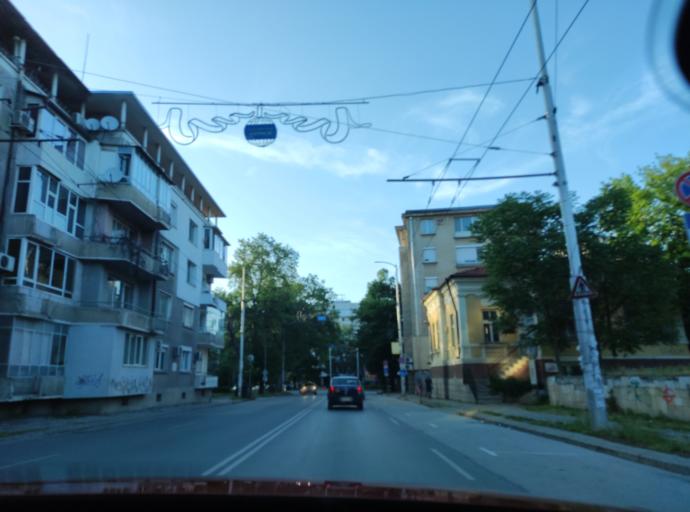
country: BG
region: Pleven
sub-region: Obshtina Pleven
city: Pleven
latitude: 43.4117
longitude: 24.6189
